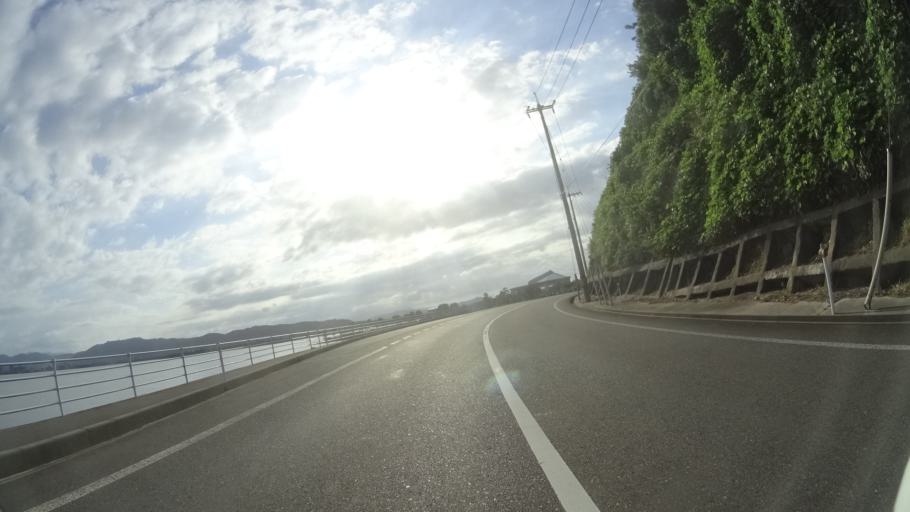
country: JP
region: Tottori
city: Kurayoshi
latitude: 35.4913
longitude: 133.8916
